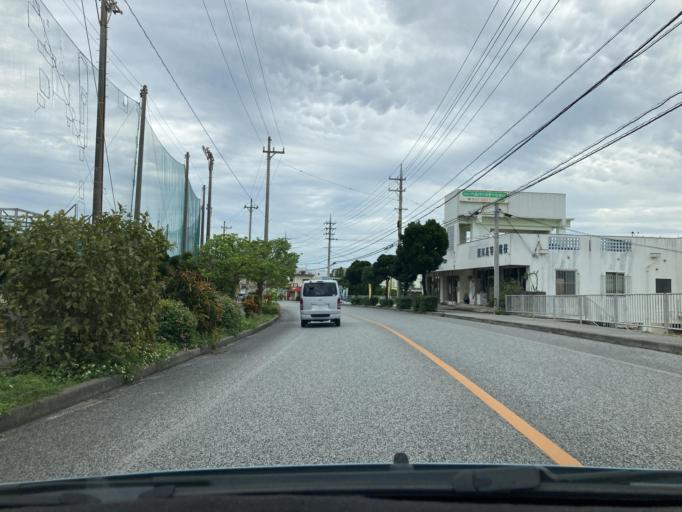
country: JP
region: Okinawa
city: Okinawa
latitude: 26.3819
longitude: 127.7507
